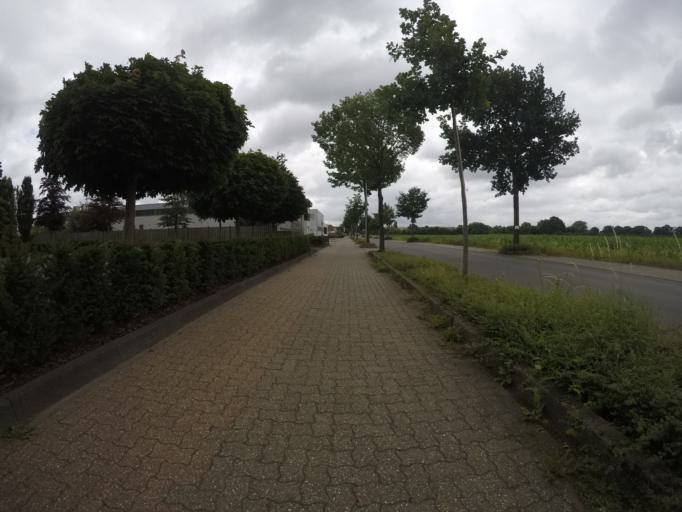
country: DE
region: North Rhine-Westphalia
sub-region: Regierungsbezirk Dusseldorf
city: Bocholt
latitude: 51.8076
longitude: 6.6016
